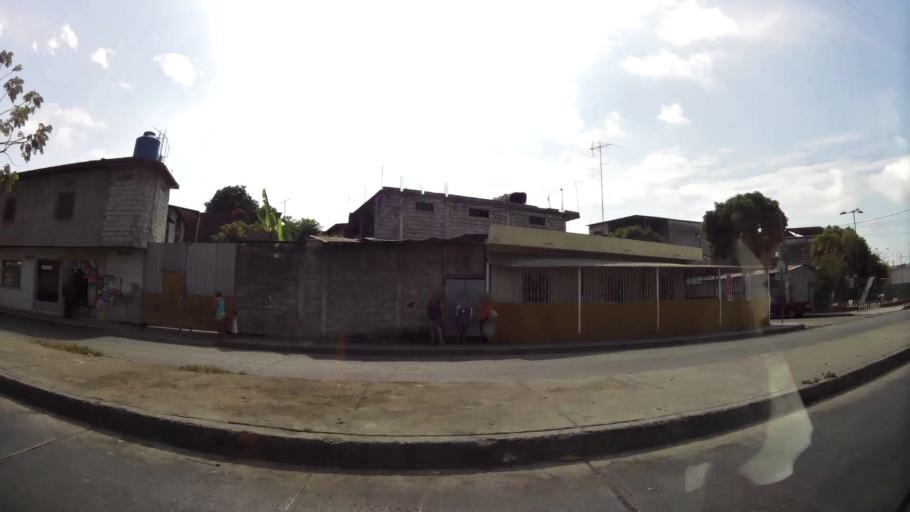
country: EC
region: Guayas
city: Guayaquil
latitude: -2.2752
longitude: -79.8873
